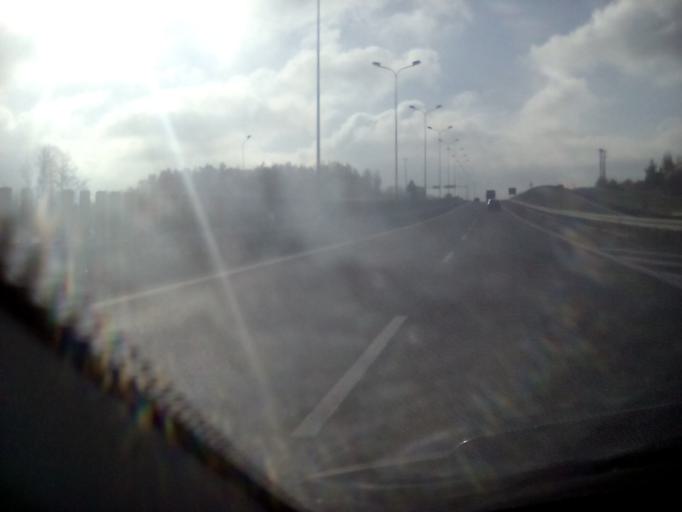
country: PL
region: Masovian Voivodeship
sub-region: Powiat grojecki
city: Goszczyn
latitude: 51.7338
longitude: 20.9154
